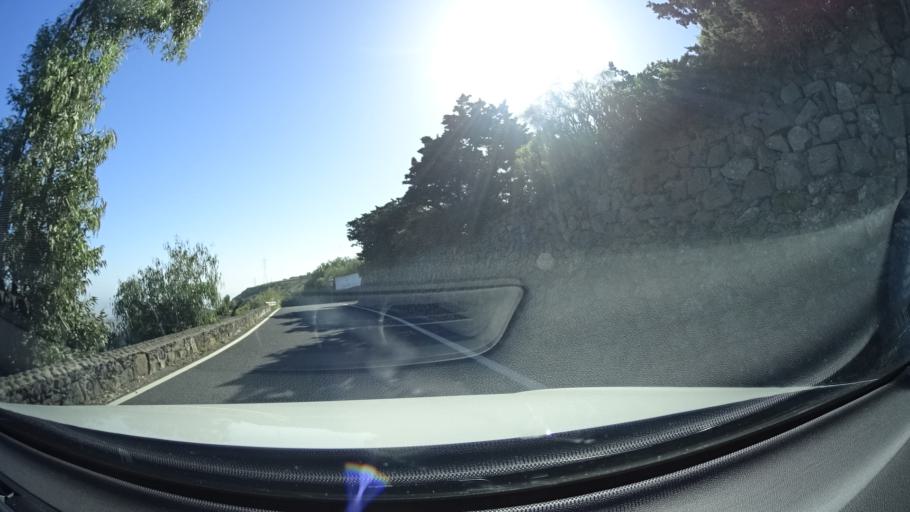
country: ES
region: Canary Islands
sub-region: Provincia de Las Palmas
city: Santa Brigida
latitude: 28.0189
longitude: -15.4595
